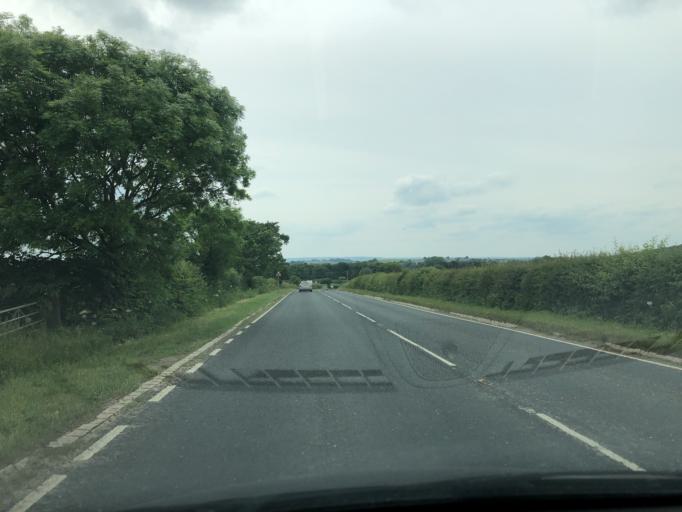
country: GB
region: England
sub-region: North Yorkshire
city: Great Habton
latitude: 54.2581
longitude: -0.8510
